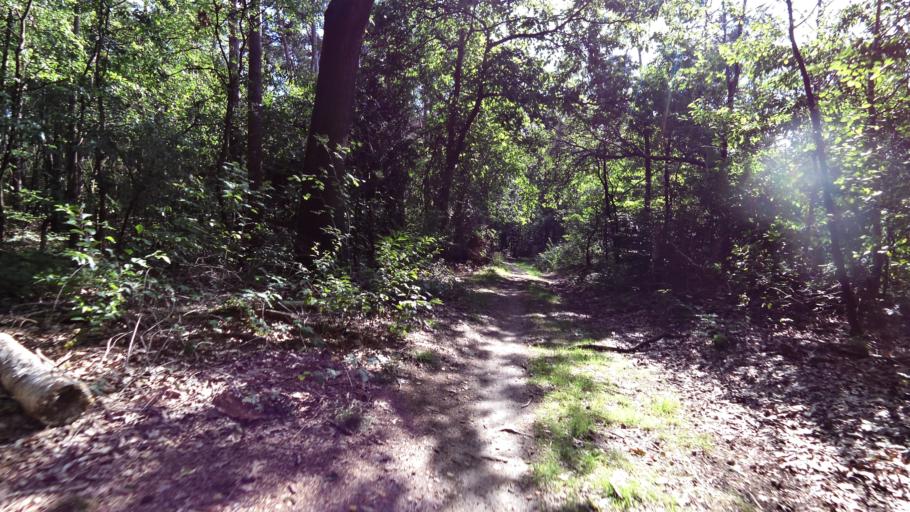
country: NL
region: Gelderland
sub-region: Gemeente Ede
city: Bennekom
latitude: 52.0113
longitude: 5.7126
